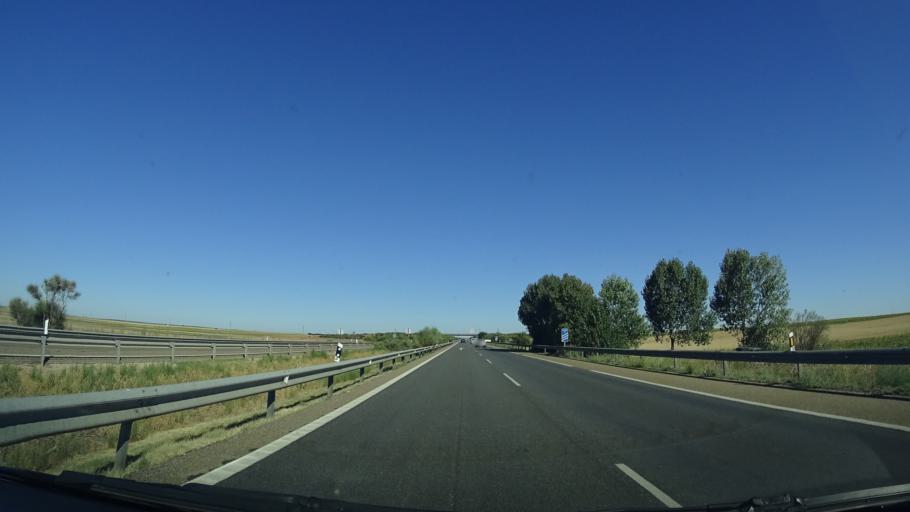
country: ES
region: Castille and Leon
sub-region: Provincia de Valladolid
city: San Pedro de Latarce
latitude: 41.7952
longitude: -5.3375
